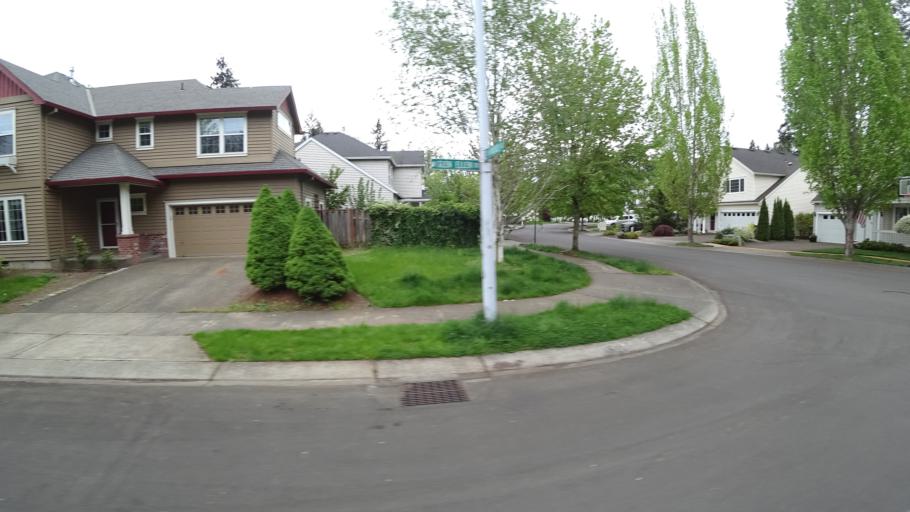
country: US
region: Oregon
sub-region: Washington County
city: Hillsboro
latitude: 45.5352
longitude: -122.9857
